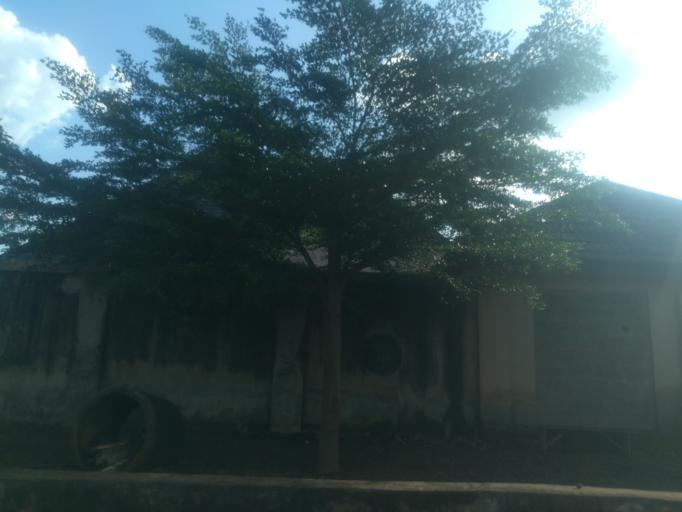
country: NG
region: Oyo
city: Ibadan
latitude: 7.4346
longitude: 3.9755
